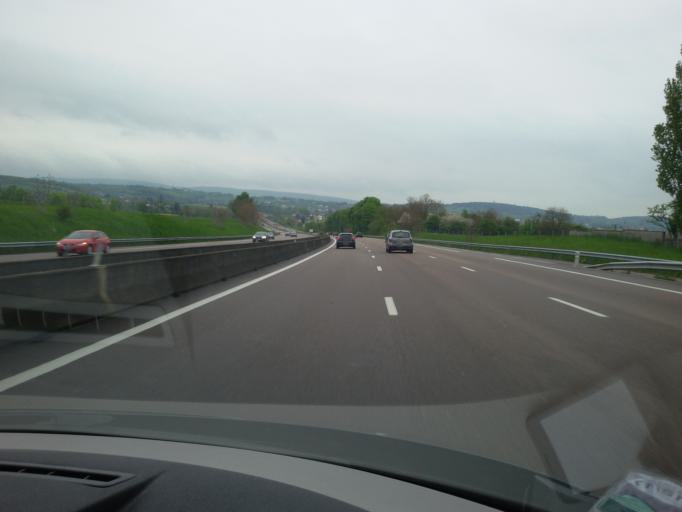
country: FR
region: Bourgogne
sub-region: Departement de Saone-et-Loire
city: Tournus
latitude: 46.5454
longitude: 4.9160
